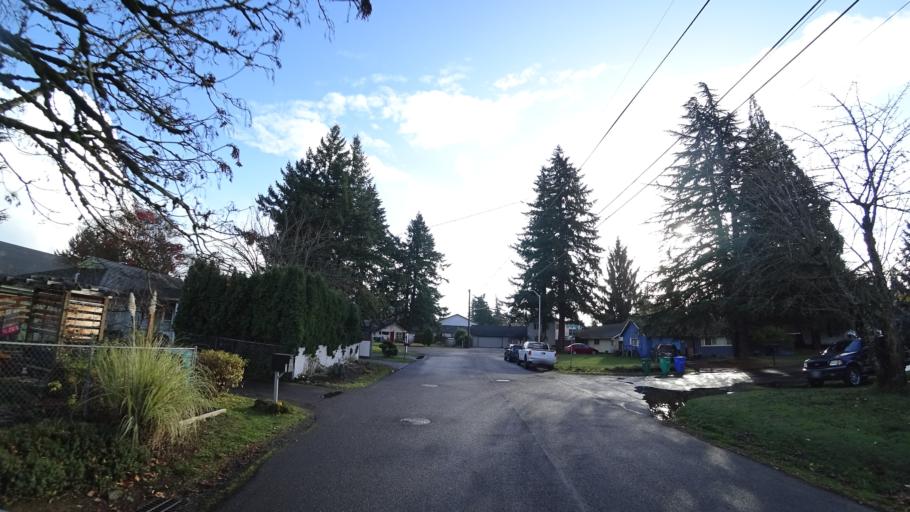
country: US
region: Oregon
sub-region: Multnomah County
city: Lents
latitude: 45.5248
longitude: -122.5423
